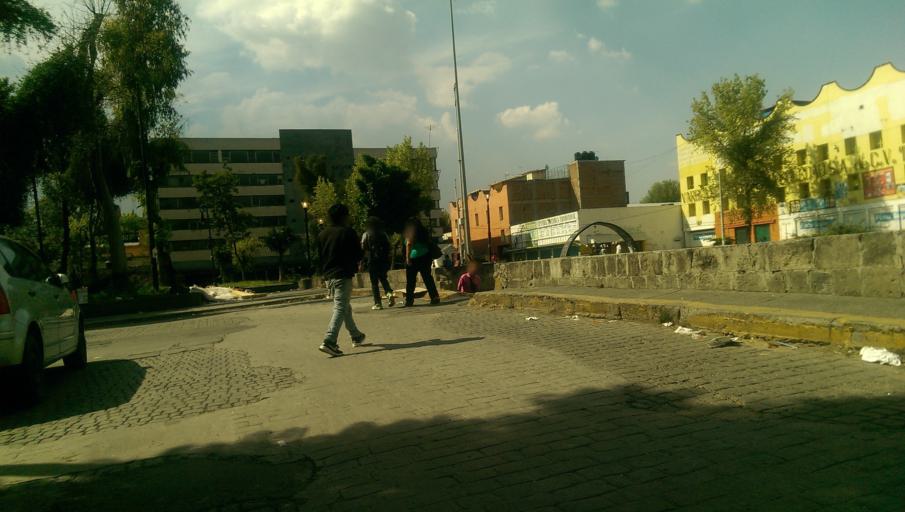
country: MX
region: Mexico City
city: Mexico City
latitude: 19.4315
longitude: -99.1232
